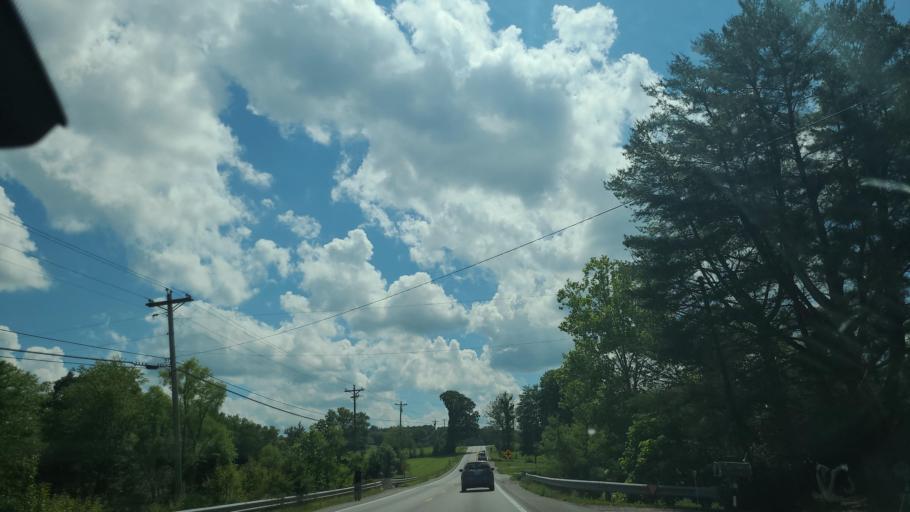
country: US
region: Kentucky
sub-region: Whitley County
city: Corbin
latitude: 36.9019
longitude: -84.1703
